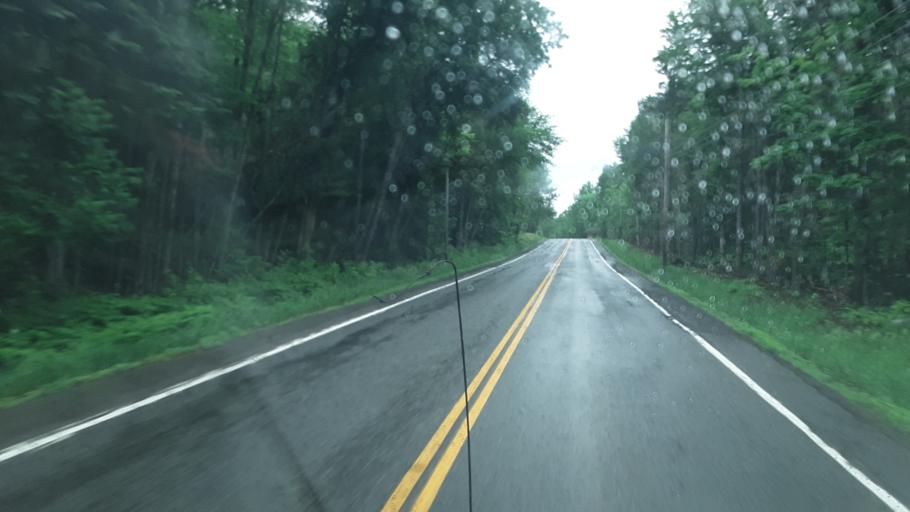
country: US
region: Maine
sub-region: Penobscot County
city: Patten
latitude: 46.1503
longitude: -68.3576
